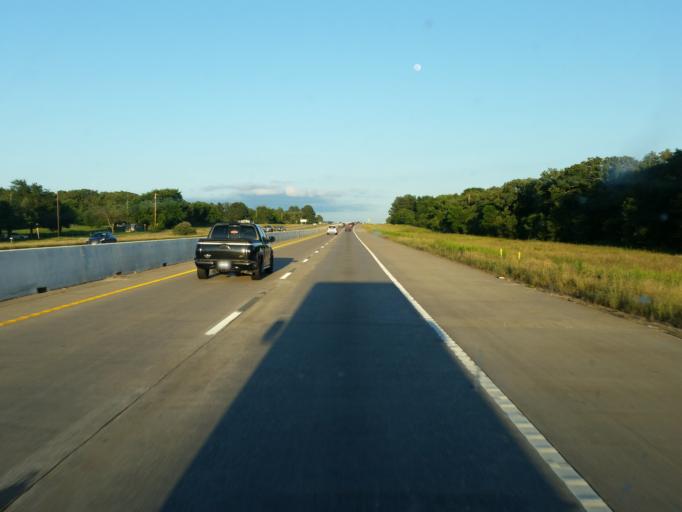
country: US
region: Texas
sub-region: Van Zandt County
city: Wills Point
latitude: 32.6133
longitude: -95.9656
